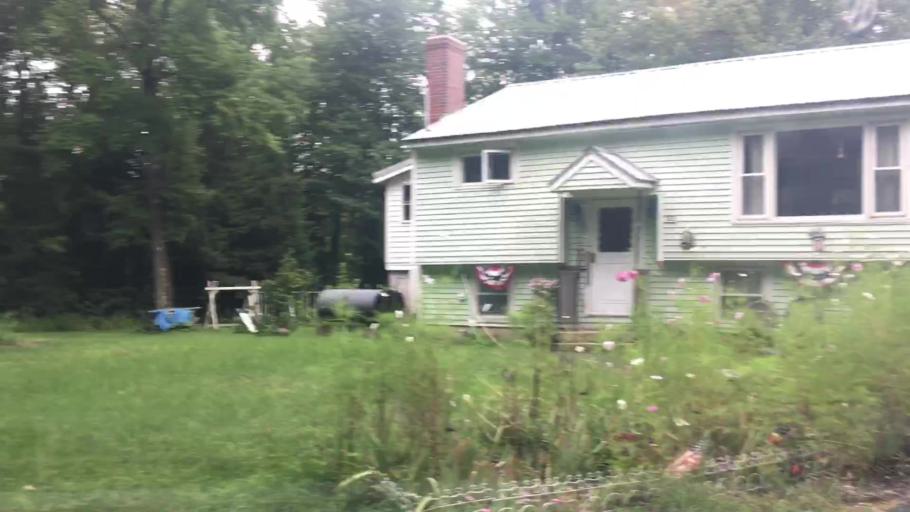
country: US
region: Maine
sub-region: York County
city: South Sanford
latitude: 43.4190
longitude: -70.6733
